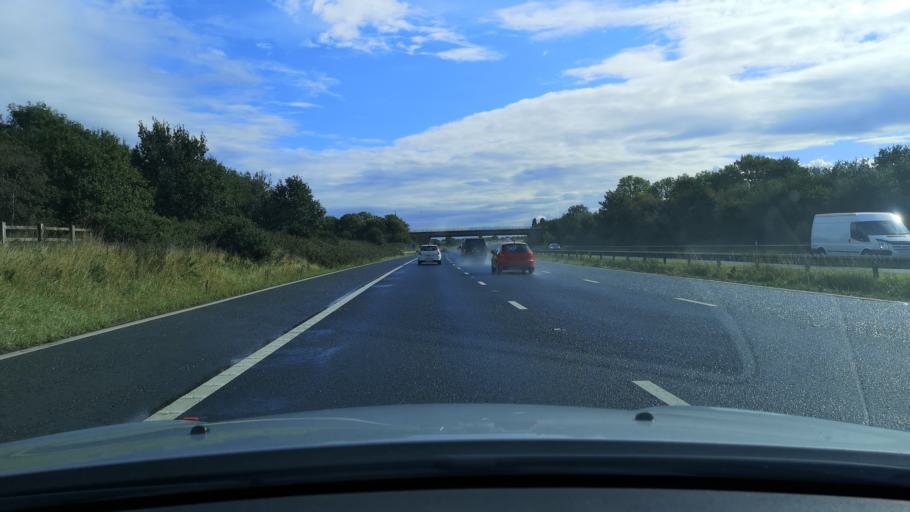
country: GB
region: England
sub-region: East Riding of Yorkshire
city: Pollington
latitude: 53.6941
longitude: -1.1235
